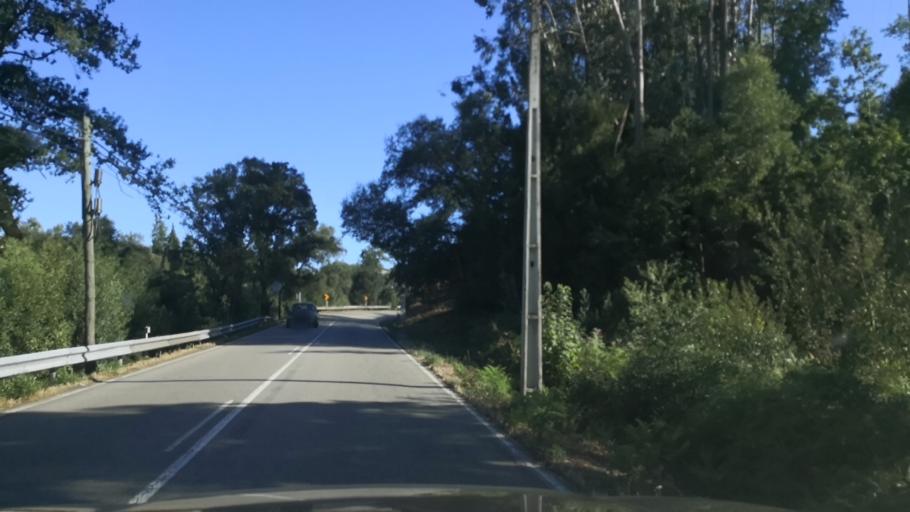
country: PT
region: Porto
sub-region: Pacos de Ferreira
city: Seroa
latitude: 41.2758
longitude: -8.4688
